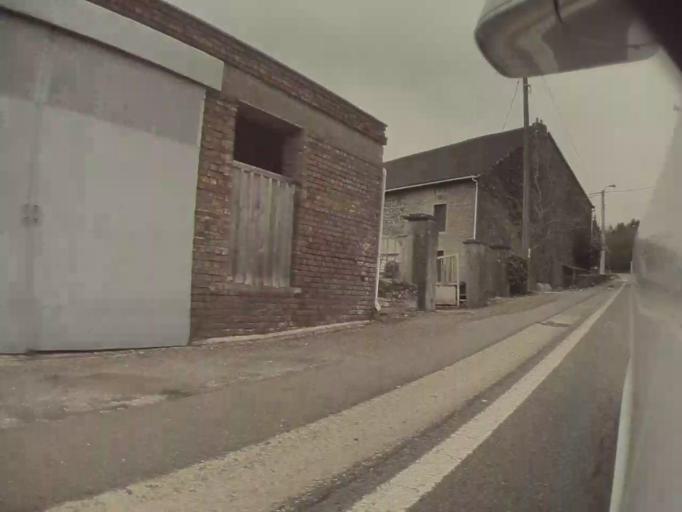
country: BE
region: Wallonia
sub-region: Province de Liege
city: Ferrieres
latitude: 50.4045
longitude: 5.6062
